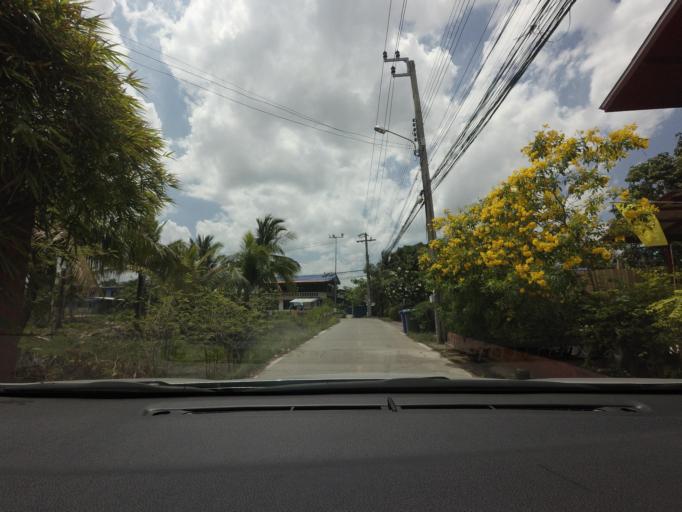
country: TH
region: Samut Prakan
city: Phra Samut Chedi
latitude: 13.6249
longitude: 100.5698
